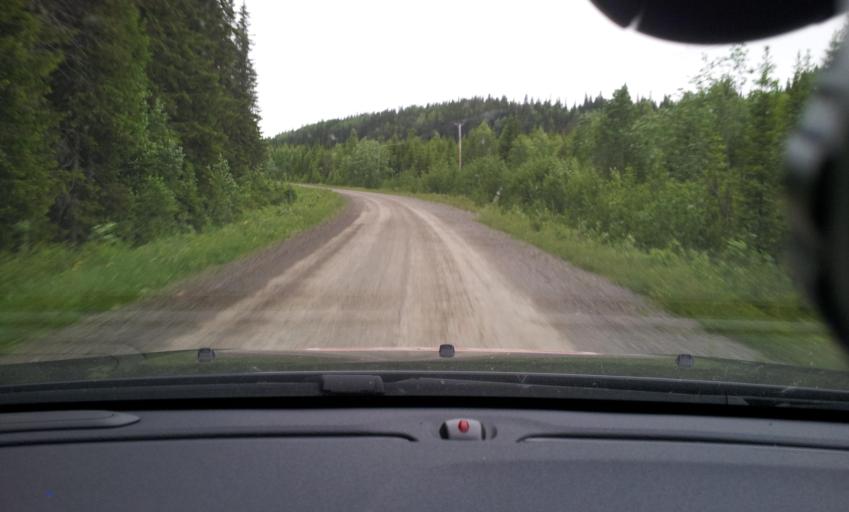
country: SE
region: Jaemtland
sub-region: Are Kommun
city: Jarpen
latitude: 63.1972
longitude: 13.6610
